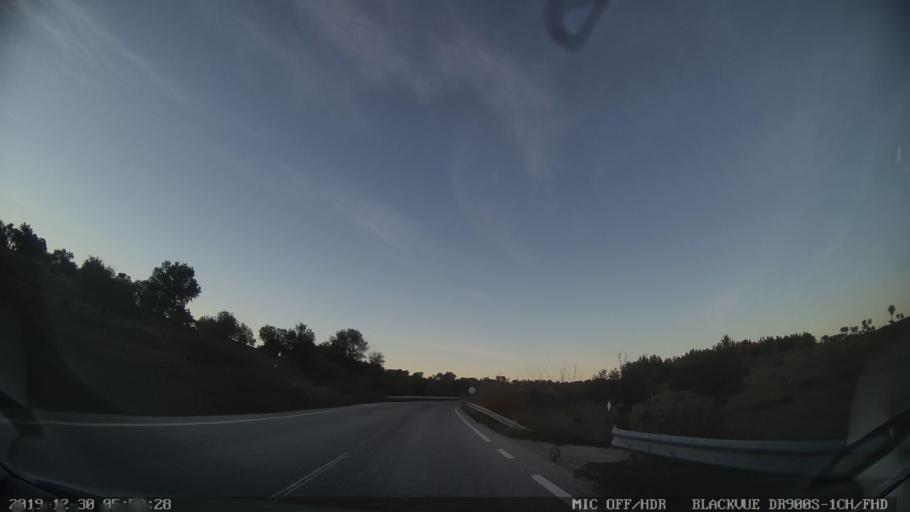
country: PT
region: Castelo Branco
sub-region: Idanha-A-Nova
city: Idanha-a-Nova
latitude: 40.0442
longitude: -7.2430
